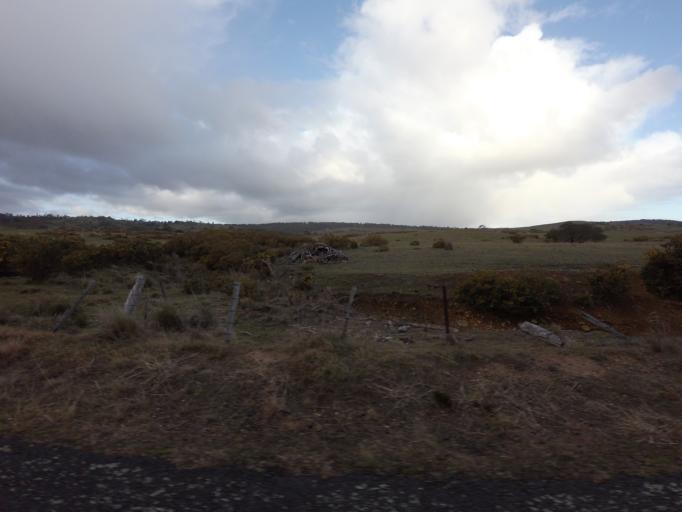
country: AU
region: Tasmania
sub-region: Break O'Day
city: St Helens
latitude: -41.9994
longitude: 148.0890
